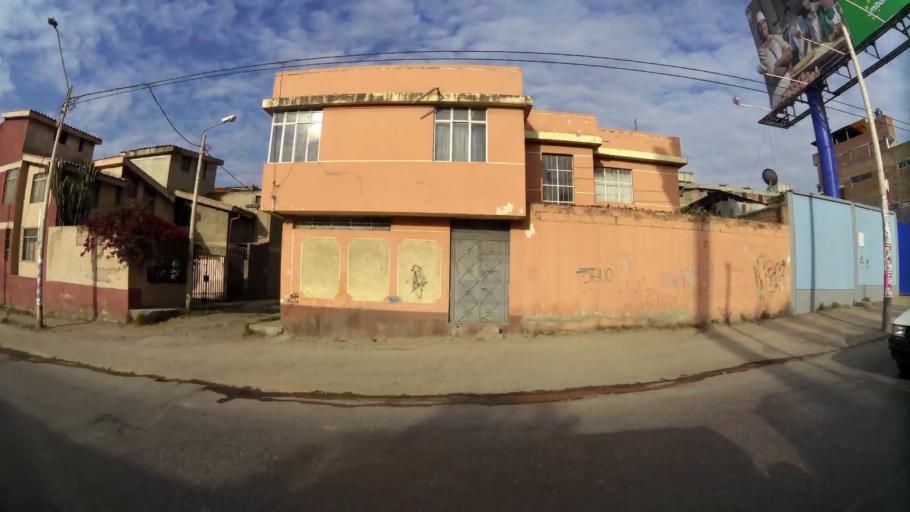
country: PE
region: Junin
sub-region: Provincia de Huancayo
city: Huancayo
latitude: -12.0601
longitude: -75.2105
